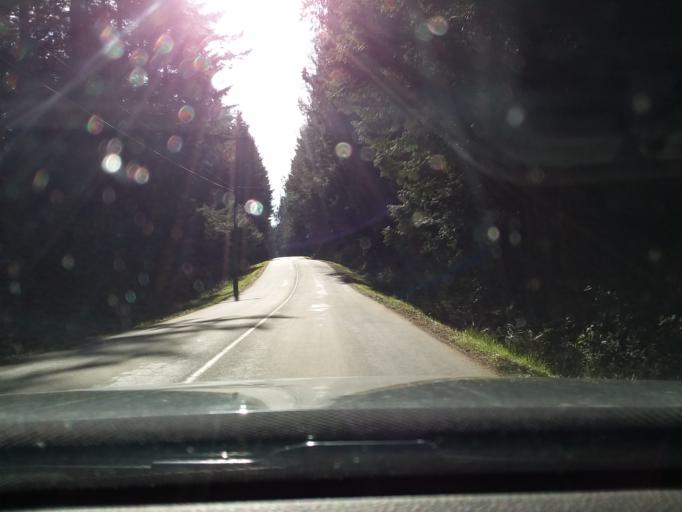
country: CA
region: British Columbia
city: North Saanich
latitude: 48.9181
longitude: -123.4342
